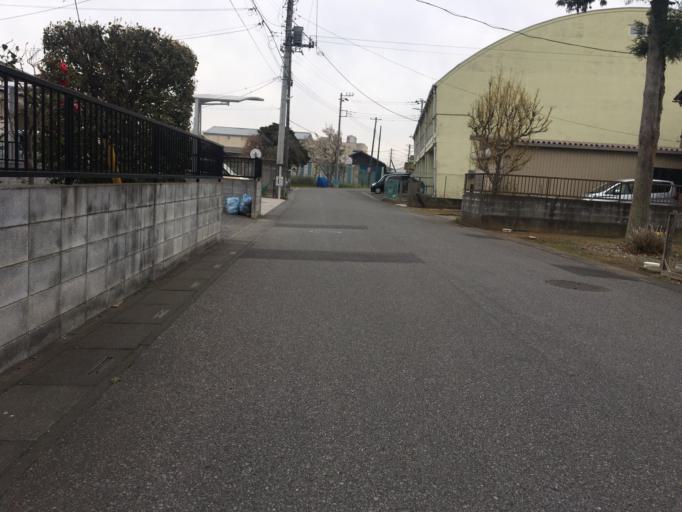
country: JP
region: Saitama
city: Kisai
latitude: 36.1039
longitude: 139.5758
